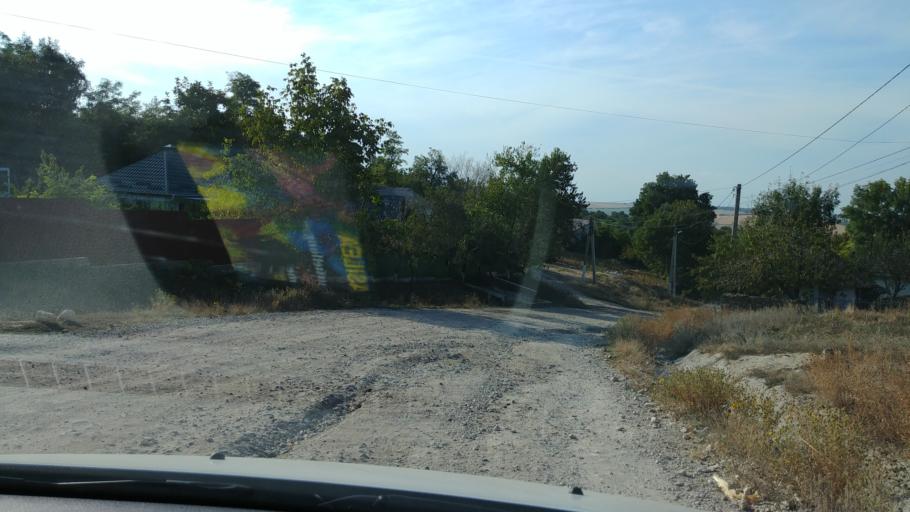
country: MD
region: Rezina
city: Rezina
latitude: 47.7457
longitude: 28.8883
